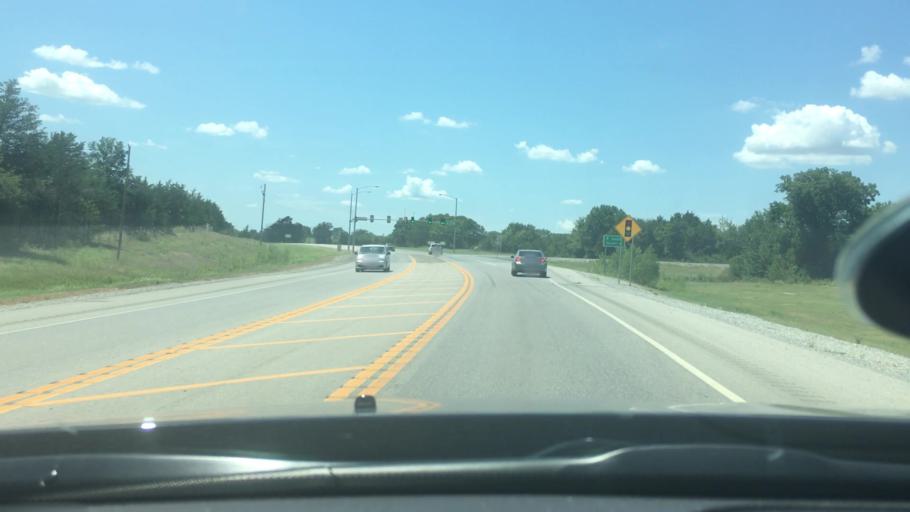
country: US
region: Oklahoma
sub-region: Bryan County
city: Durant
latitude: 33.9969
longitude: -96.3344
